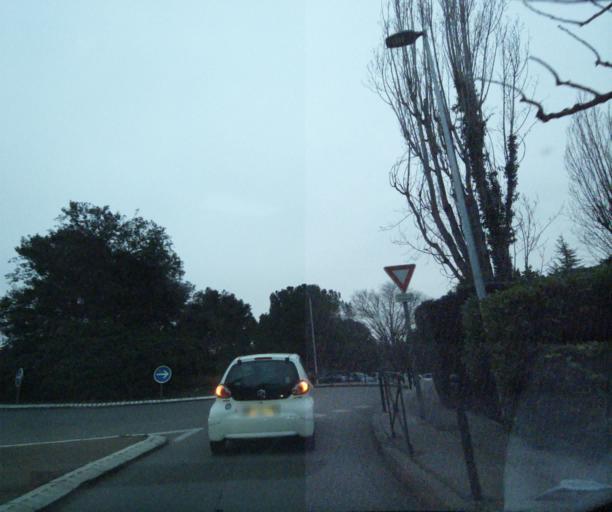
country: FR
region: Provence-Alpes-Cote d'Azur
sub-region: Departement des Bouches-du-Rhone
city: Aix-en-Provence
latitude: 43.5231
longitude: 5.4685
